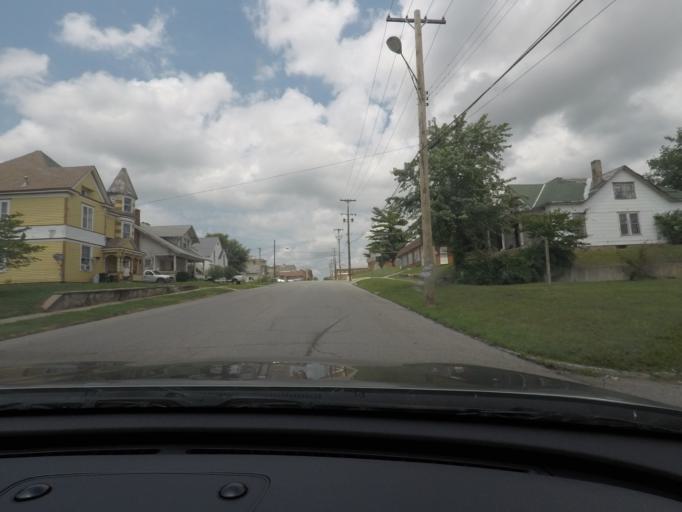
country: US
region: Missouri
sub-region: Carroll County
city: Carrollton
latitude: 39.3548
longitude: -93.4960
